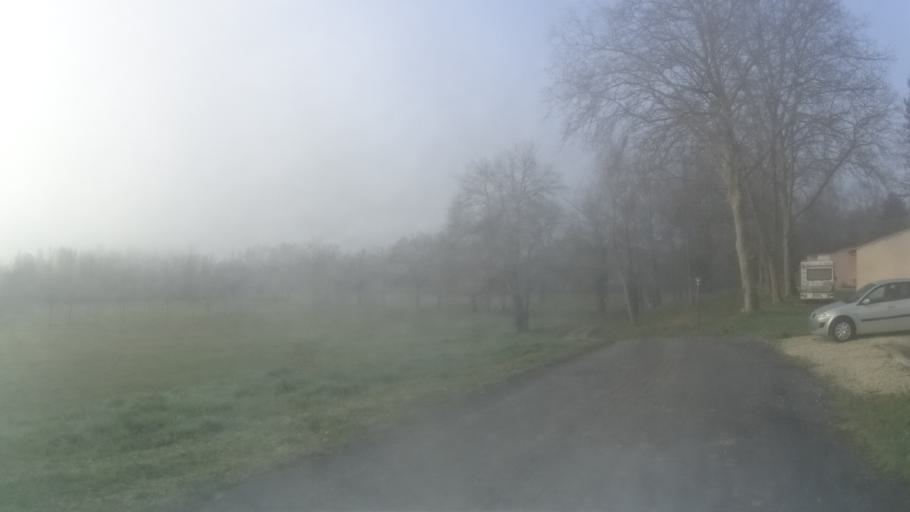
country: FR
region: Poitou-Charentes
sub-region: Departement de la Charente-Maritime
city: Saint-Aigulin
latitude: 45.1518
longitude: -0.0133
